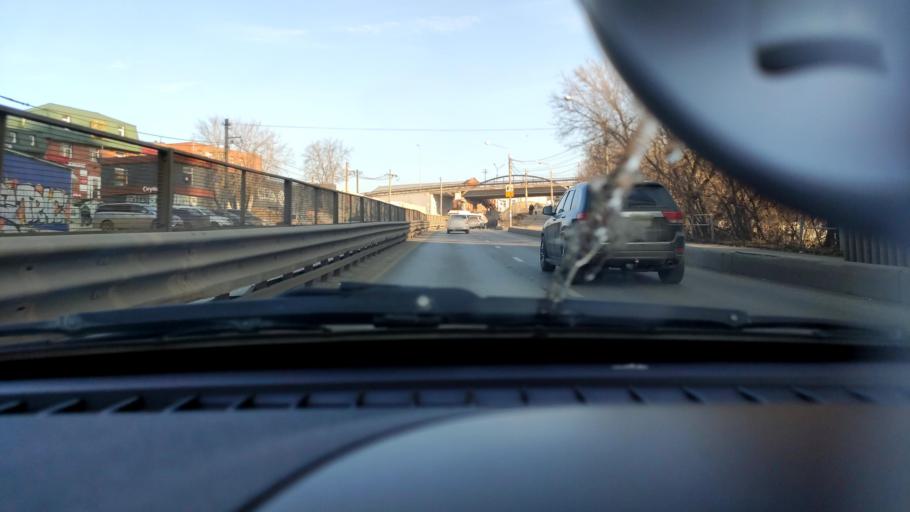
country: RU
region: Perm
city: Perm
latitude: 57.9990
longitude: 56.2256
